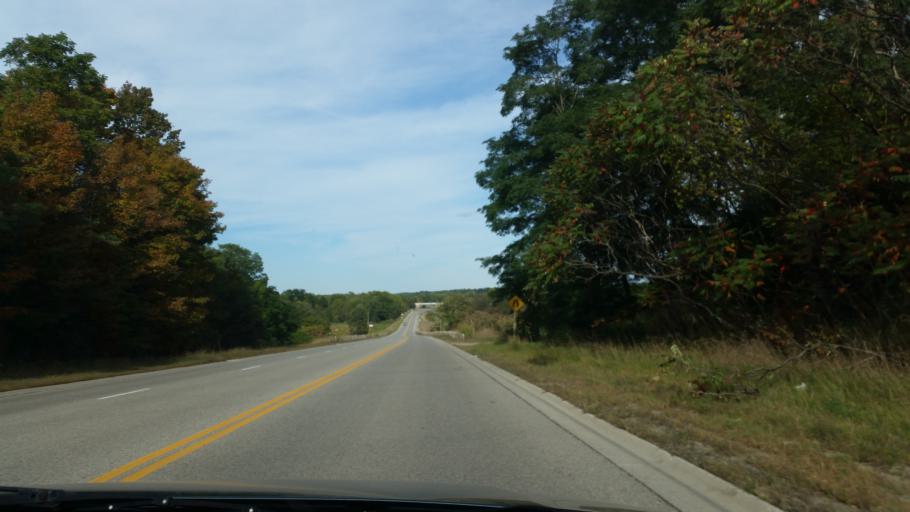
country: CA
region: Ontario
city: Delaware
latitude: 42.8932
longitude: -81.4413
